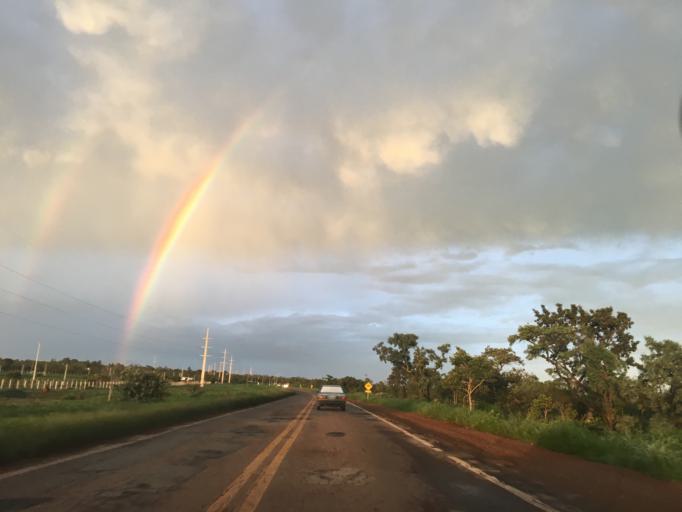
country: BR
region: Federal District
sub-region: Brasilia
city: Brasilia
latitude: -15.9744
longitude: -47.9738
